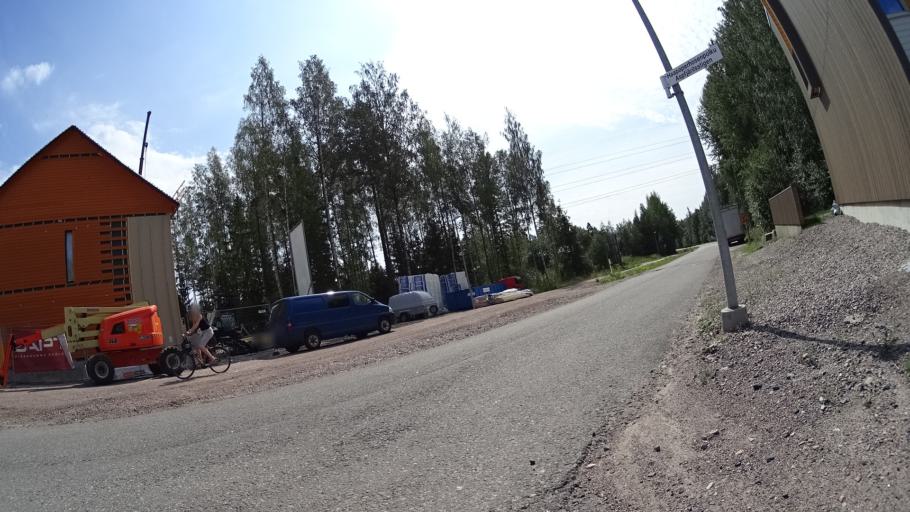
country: FI
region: Uusimaa
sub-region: Helsinki
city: Teekkarikylae
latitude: 60.2550
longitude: 24.8464
